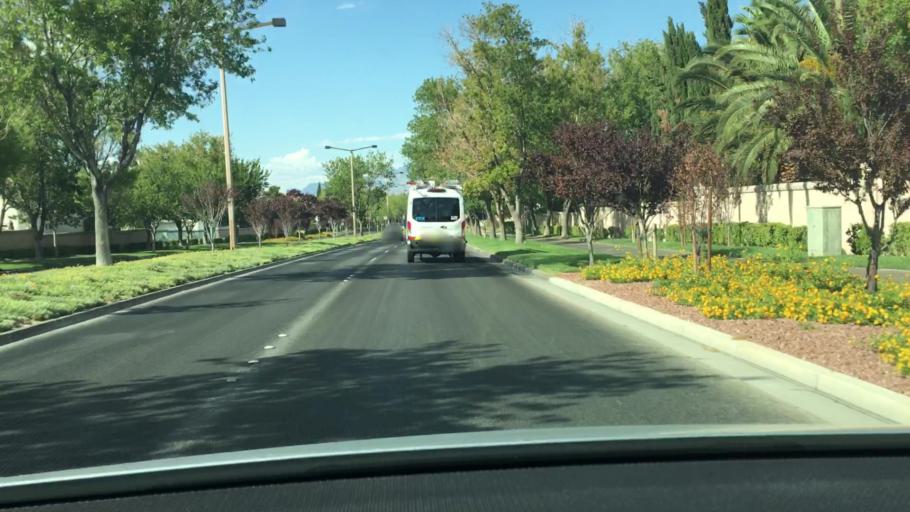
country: US
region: Nevada
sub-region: Clark County
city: Summerlin South
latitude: 36.2009
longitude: -115.3005
